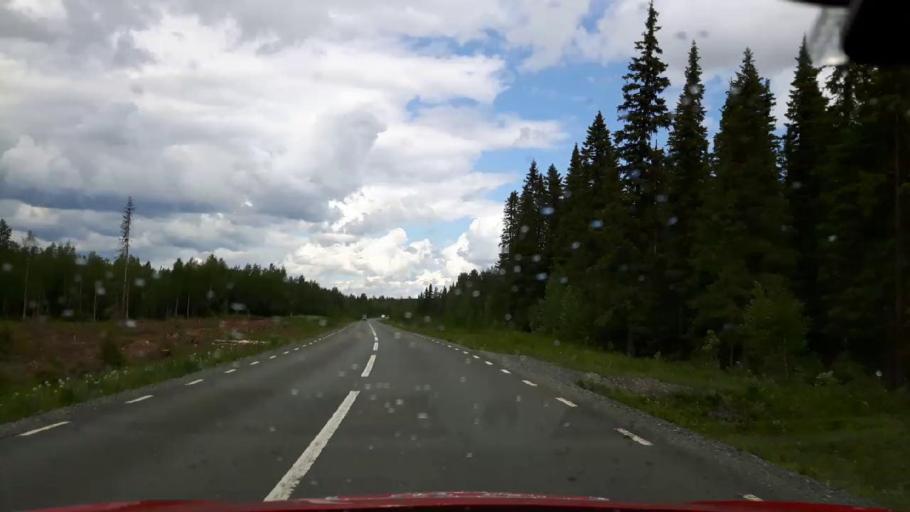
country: SE
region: Jaemtland
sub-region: Krokoms Kommun
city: Krokom
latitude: 63.5834
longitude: 14.2930
